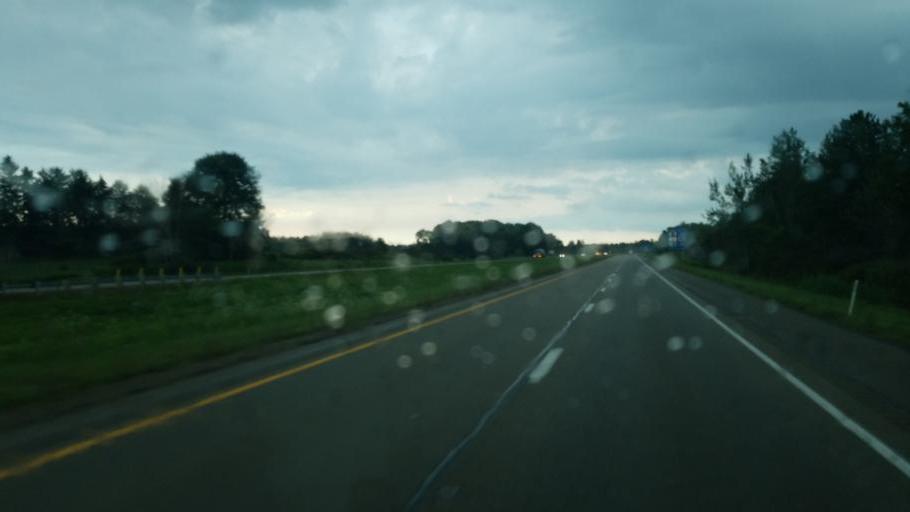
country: US
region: Pennsylvania
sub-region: Mercer County
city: Grove City
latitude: 41.1595
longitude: -80.1596
